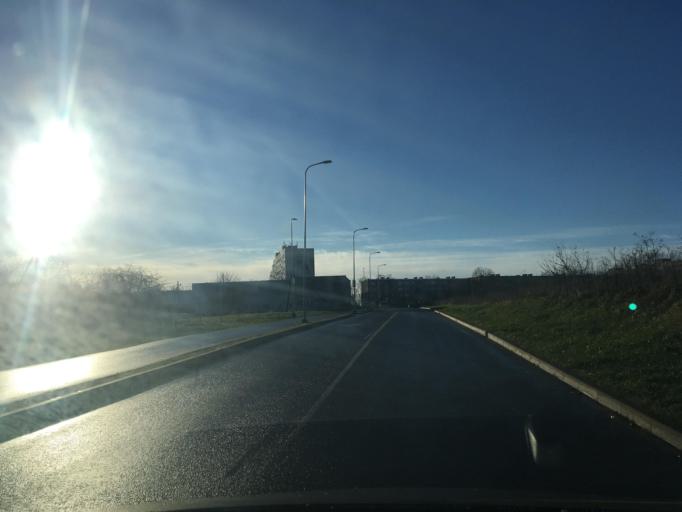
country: EE
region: Ida-Virumaa
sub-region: Narva linn
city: Narva
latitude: 59.3837
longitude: 28.1714
